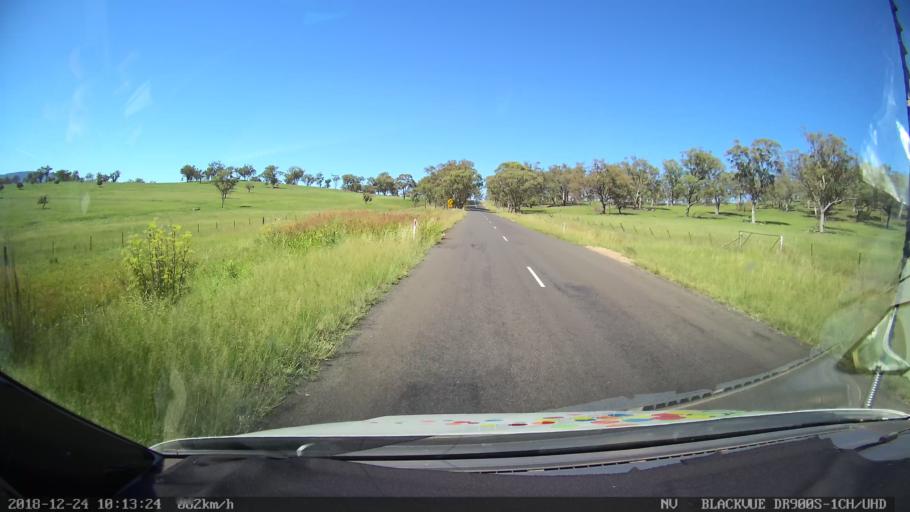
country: AU
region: New South Wales
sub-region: Liverpool Plains
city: Quirindi
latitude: -31.6895
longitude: 150.6399
